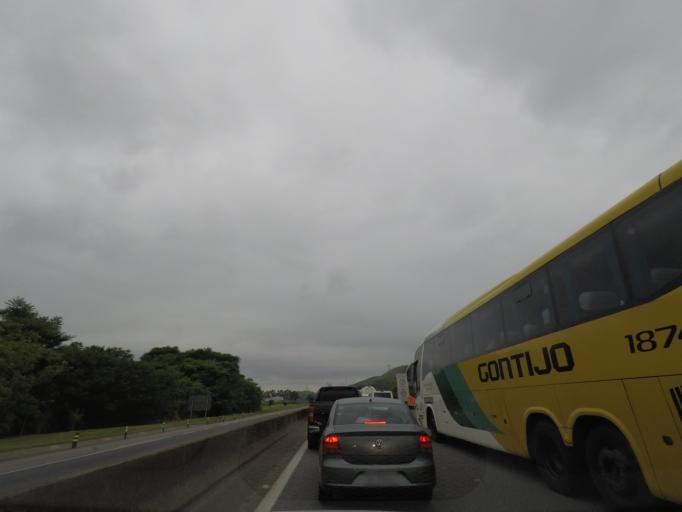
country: BR
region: Sao Paulo
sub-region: Aparecida
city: Aparecida
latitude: -22.8902
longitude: -45.2890
